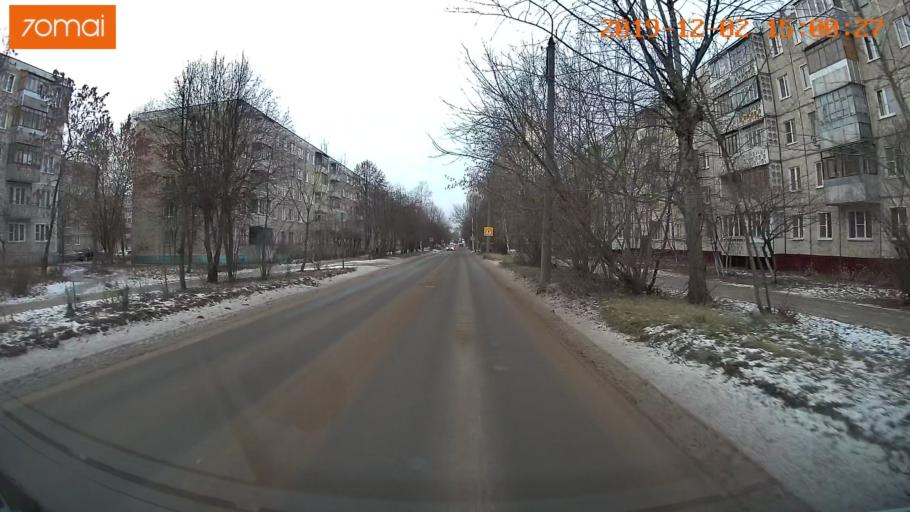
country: RU
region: Ivanovo
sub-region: Gorod Ivanovo
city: Ivanovo
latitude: 56.9703
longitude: 41.0038
